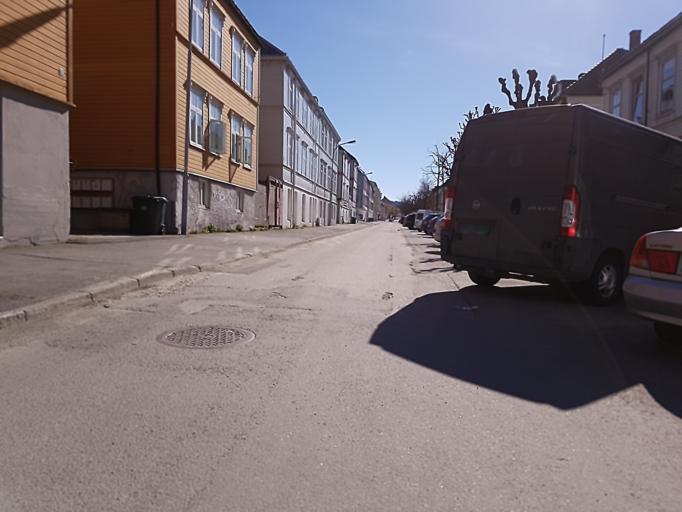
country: NO
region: Sor-Trondelag
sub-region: Trondheim
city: Trondheim
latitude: 63.4335
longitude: 10.4161
